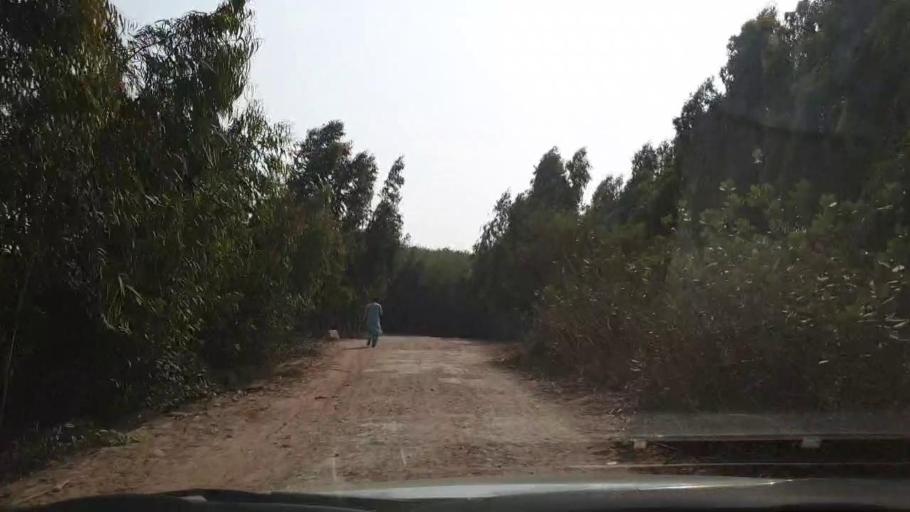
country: PK
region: Sindh
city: Matiari
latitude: 25.6482
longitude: 68.5533
